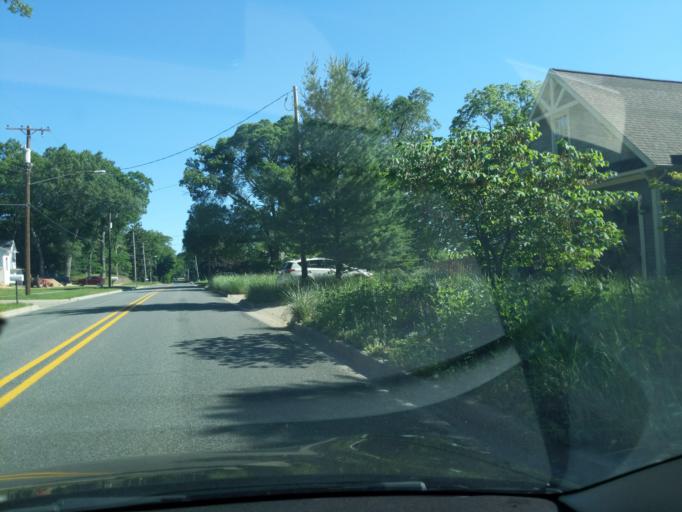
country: US
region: Michigan
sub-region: Muskegon County
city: Montague
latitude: 43.4060
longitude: -86.3599
